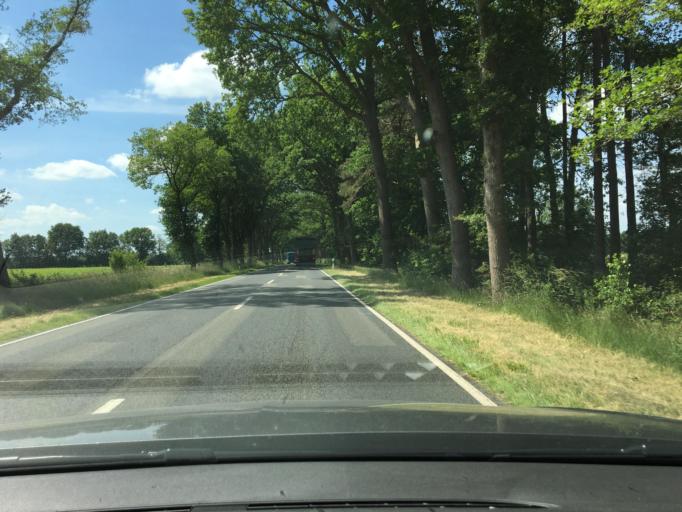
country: DE
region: Lower Saxony
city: Zeven
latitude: 53.2528
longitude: 9.2395
